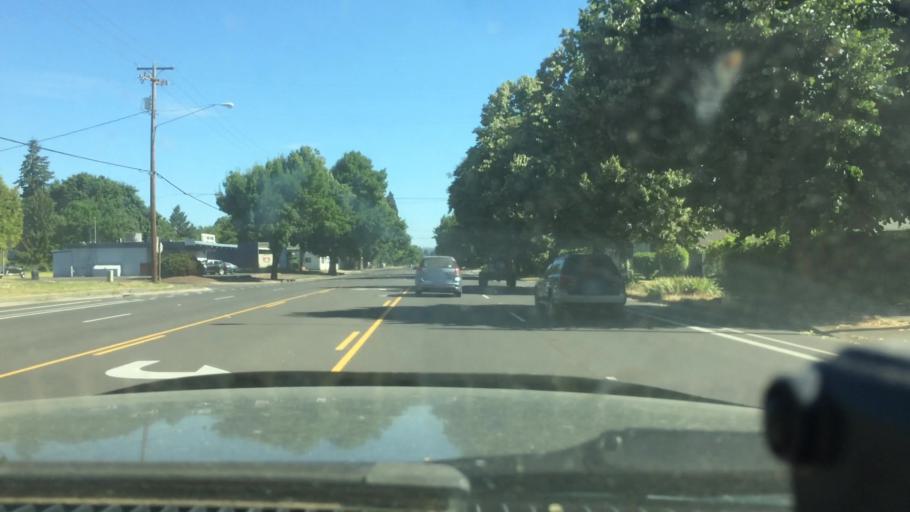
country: US
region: Oregon
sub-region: Lane County
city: Eugene
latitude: 44.0875
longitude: -123.1247
